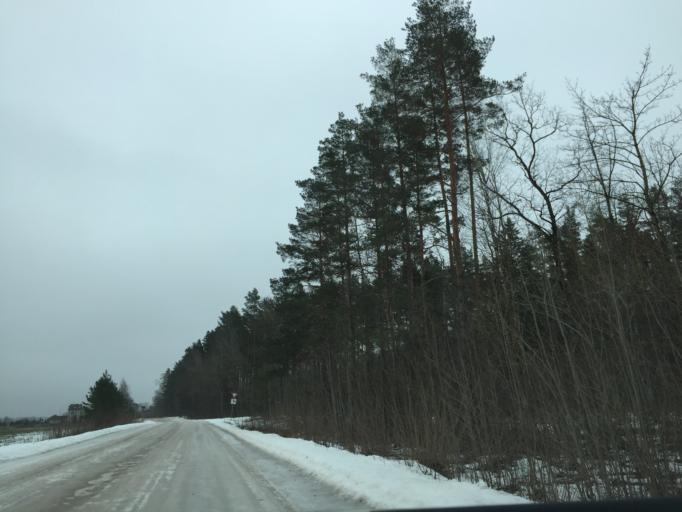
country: LV
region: Ozolnieku
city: Ozolnieki
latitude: 56.6305
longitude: 23.8153
